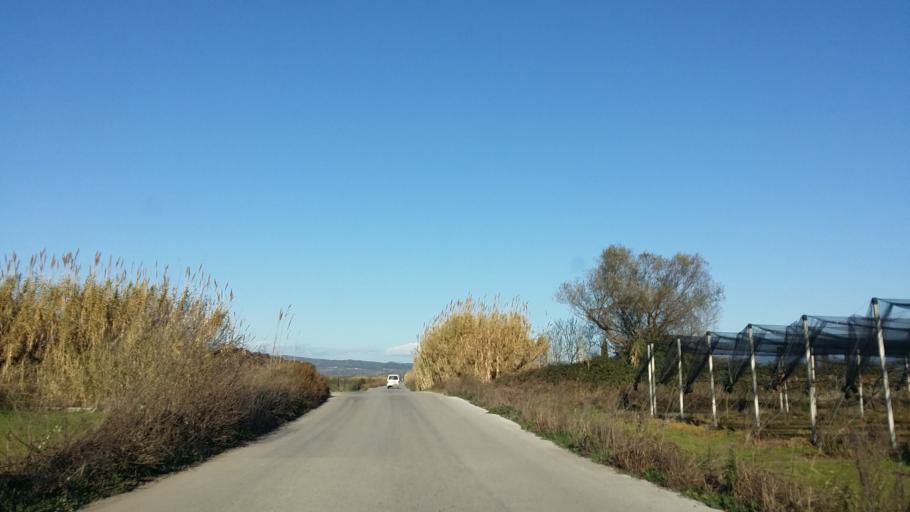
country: GR
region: West Greece
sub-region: Nomos Aitolias kai Akarnanias
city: Lepenou
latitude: 38.6428
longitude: 21.2510
